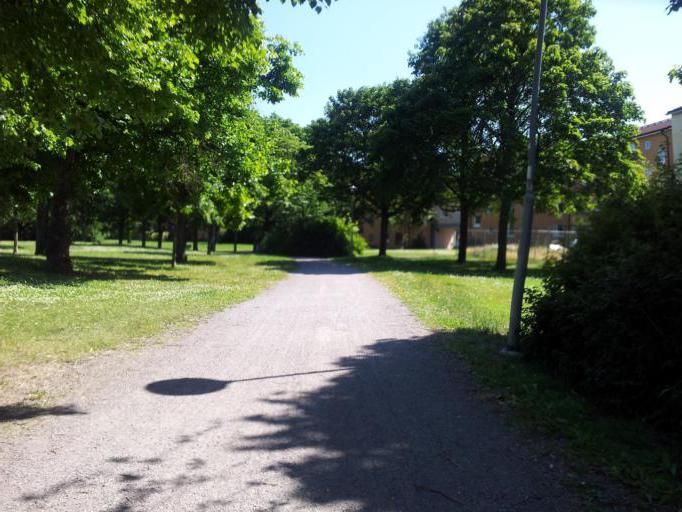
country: SE
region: Uppsala
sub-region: Uppsala Kommun
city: Uppsala
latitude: 59.8685
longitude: 17.6723
